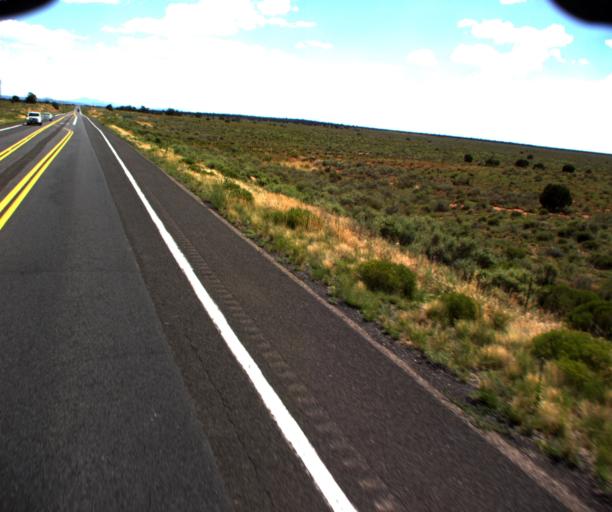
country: US
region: Arizona
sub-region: Coconino County
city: Grand Canyon Village
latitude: 35.7060
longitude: -112.1322
